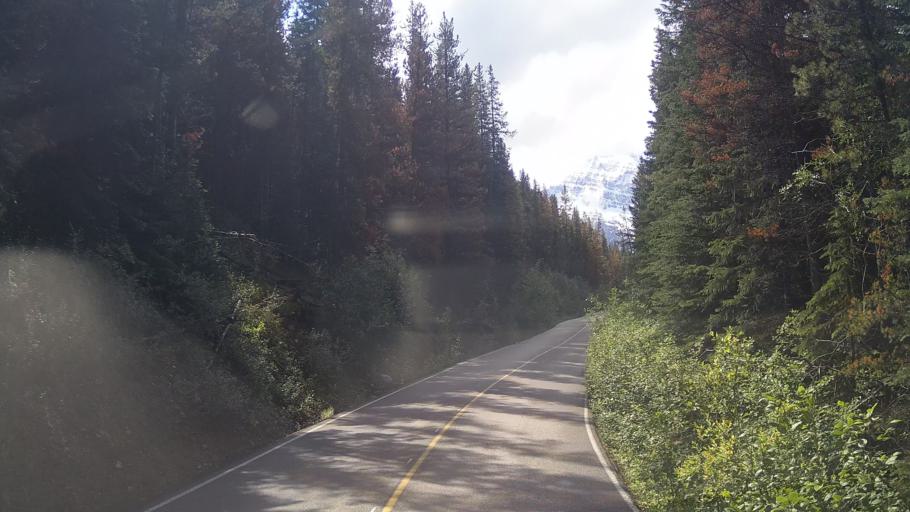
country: CA
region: Alberta
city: Jasper Park Lodge
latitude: 52.7475
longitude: -118.0468
